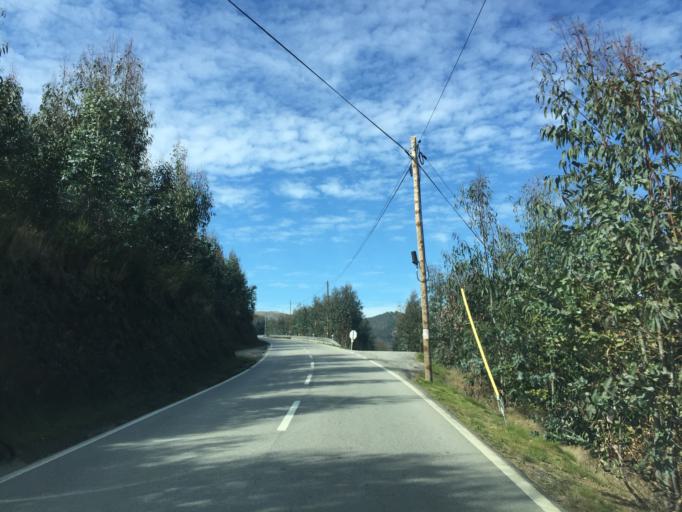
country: PT
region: Aveiro
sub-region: Arouca
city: Arouca
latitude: 40.9609
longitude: -8.2058
